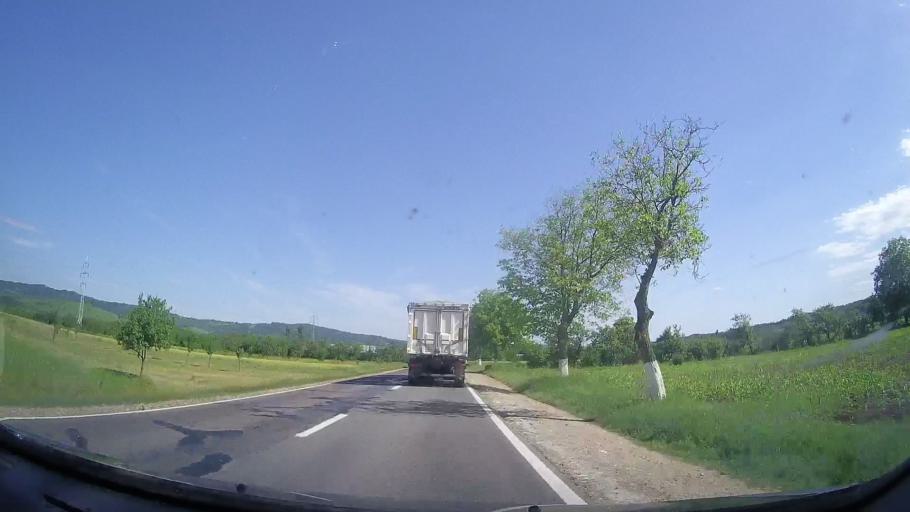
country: RO
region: Prahova
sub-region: Comuna Izvoarele
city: Homoraciu
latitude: 45.2441
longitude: 26.0259
